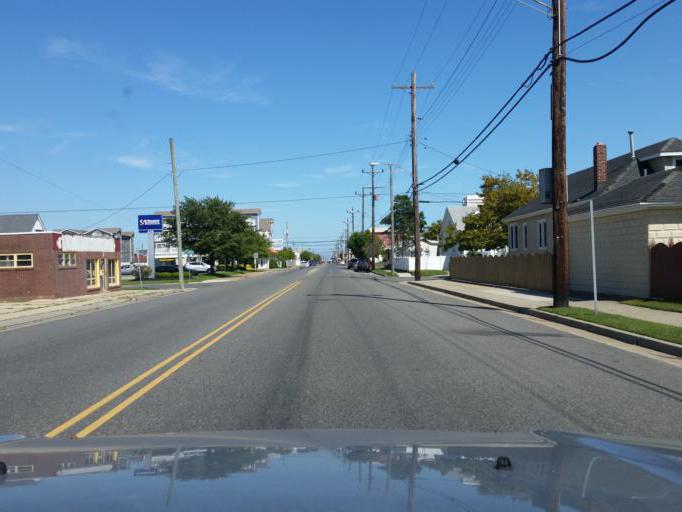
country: US
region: New Jersey
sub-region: Cape May County
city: North Wildwood
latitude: 38.9971
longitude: -74.8067
